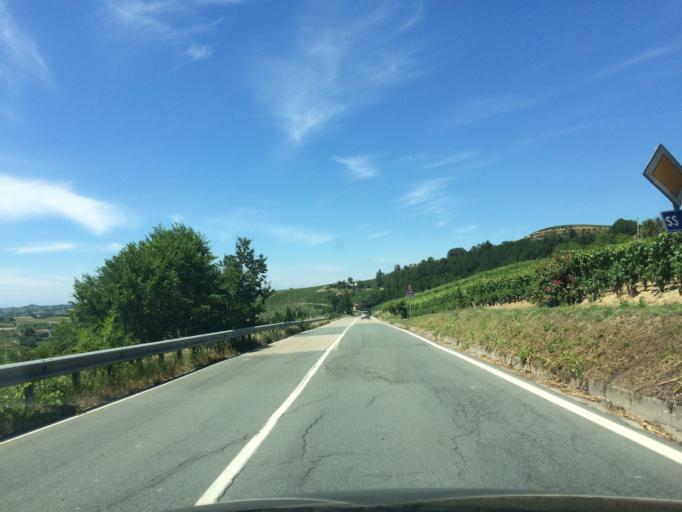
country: IT
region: Piedmont
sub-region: Provincia di Asti
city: Castel Boglione
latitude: 44.7442
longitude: 8.3852
